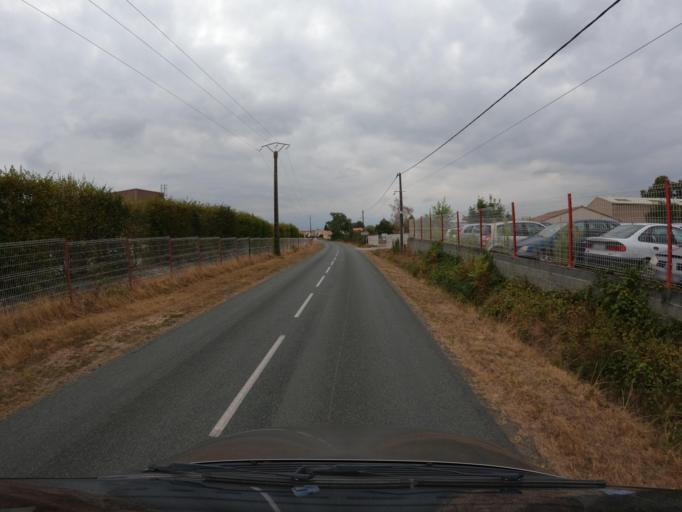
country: FR
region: Pays de la Loire
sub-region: Departement de la Vendee
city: Tiffauges
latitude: 47.0071
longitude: -1.1054
